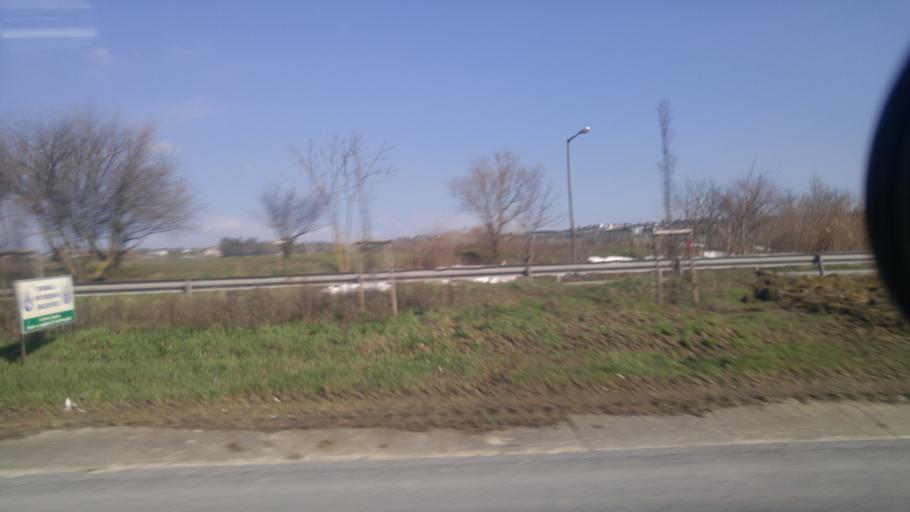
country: TR
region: Istanbul
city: Ortakoy
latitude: 41.0867
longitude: 28.3674
